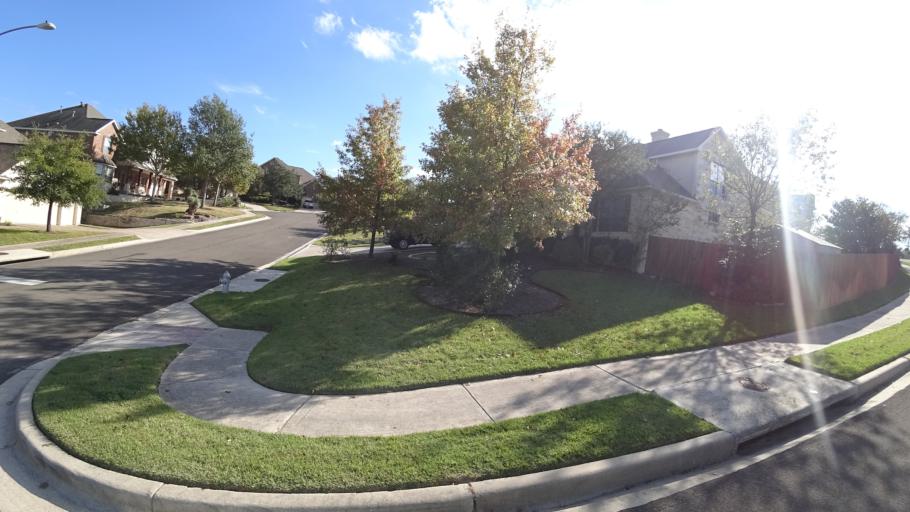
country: US
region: Texas
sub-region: Travis County
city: Barton Creek
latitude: 30.2482
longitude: -97.8723
